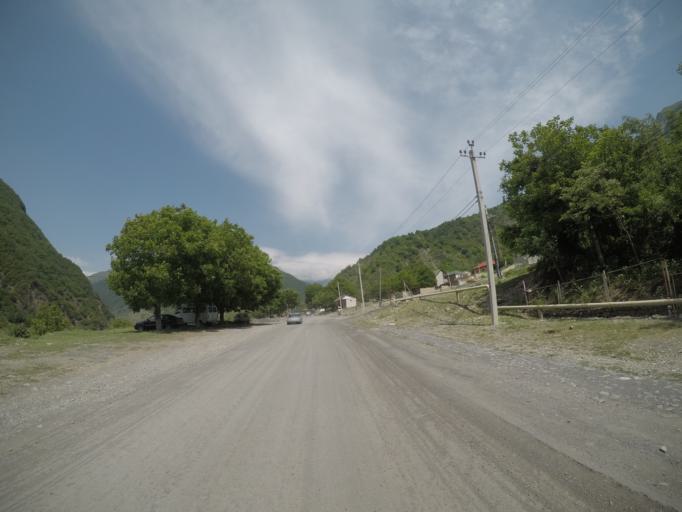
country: AZ
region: Qakh Rayon
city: Qaxbas
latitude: 41.4660
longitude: 47.0477
